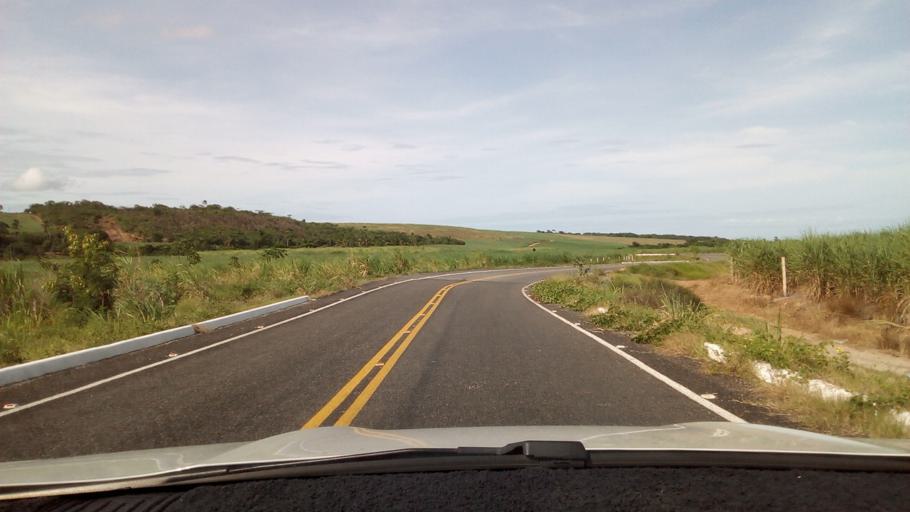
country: BR
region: Paraiba
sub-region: Joao Pessoa
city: Joao Pessoa
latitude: -7.0509
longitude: -34.8965
